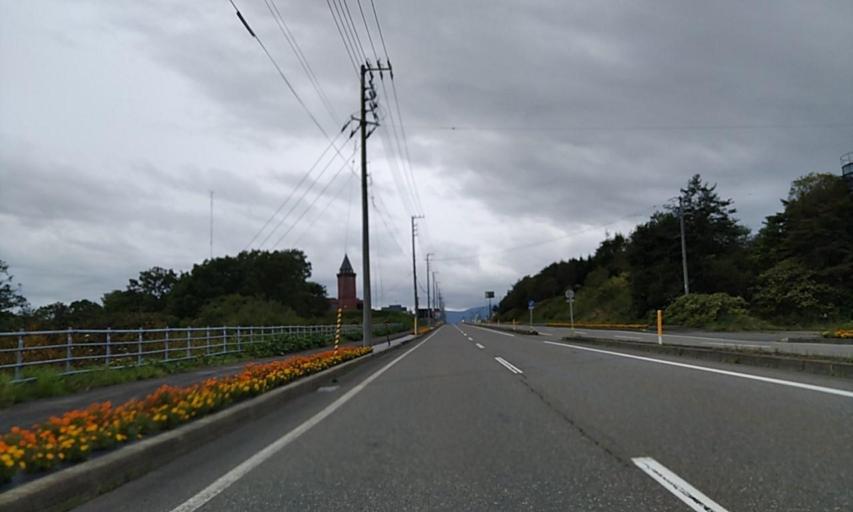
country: JP
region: Hokkaido
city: Obihiro
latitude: 42.3096
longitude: 143.3203
